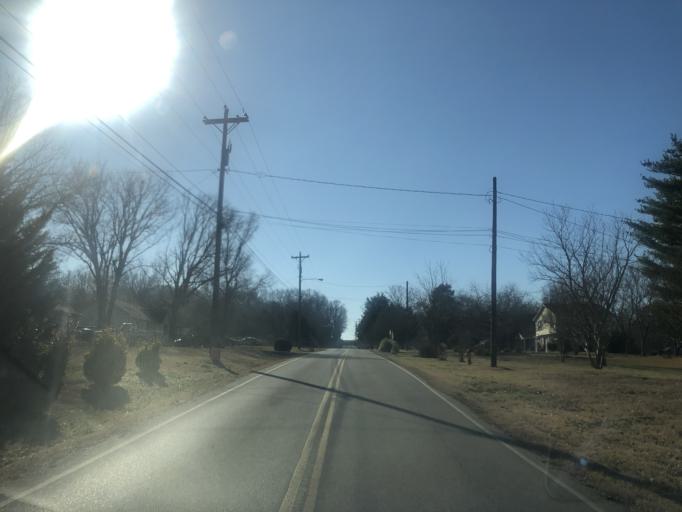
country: US
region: Tennessee
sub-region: Rutherford County
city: La Vergne
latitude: 36.0103
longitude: -86.5827
